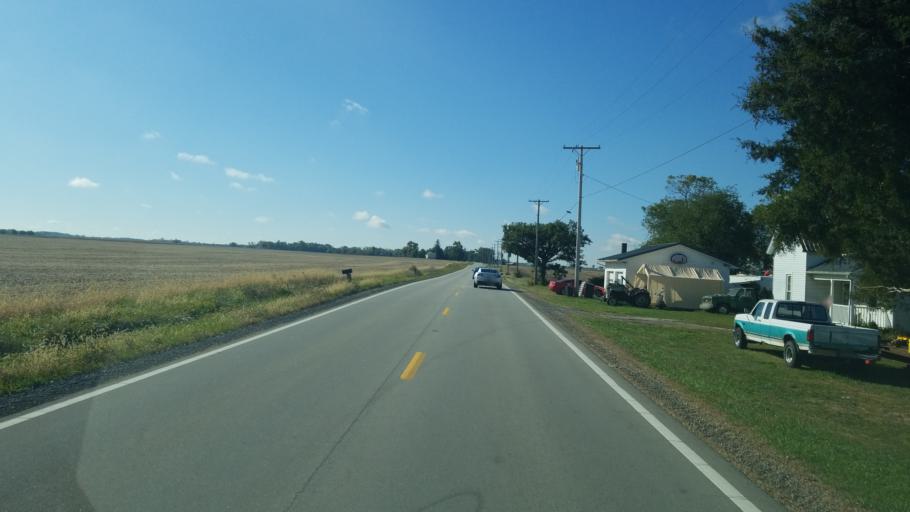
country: US
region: Ohio
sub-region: Fayette County
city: Washington Court House
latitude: 39.4694
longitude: -83.4859
